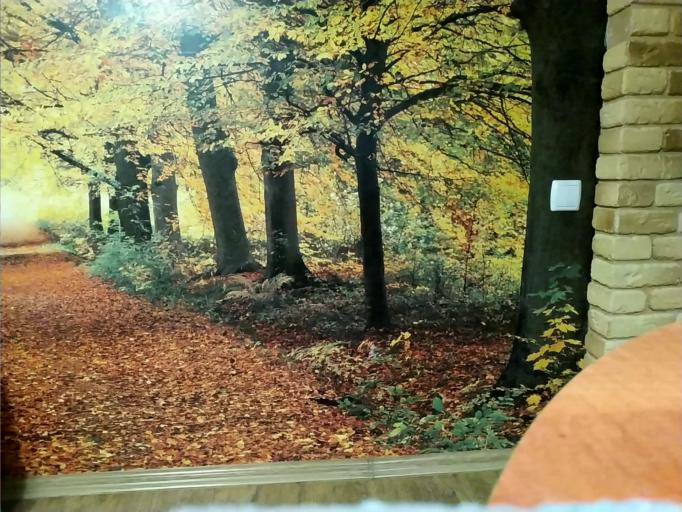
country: BY
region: Minsk
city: Plyeshchanitsy
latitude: 54.4275
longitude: 27.6095
